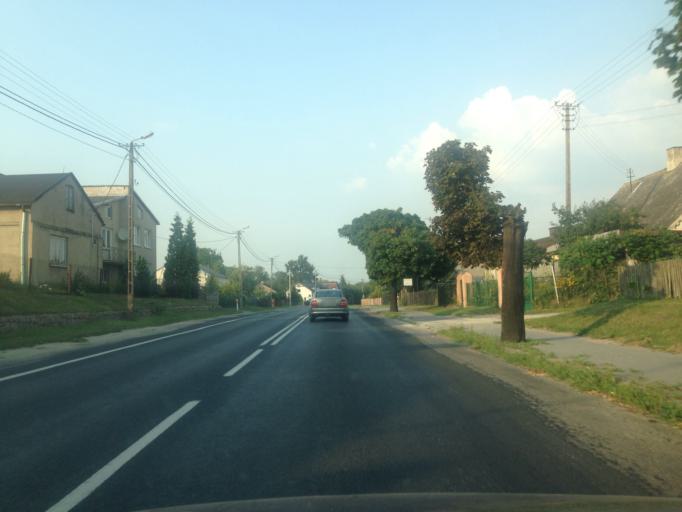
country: PL
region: Kujawsko-Pomorskie
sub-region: Powiat lipnowski
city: Lipno
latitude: 52.8095
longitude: 19.1353
